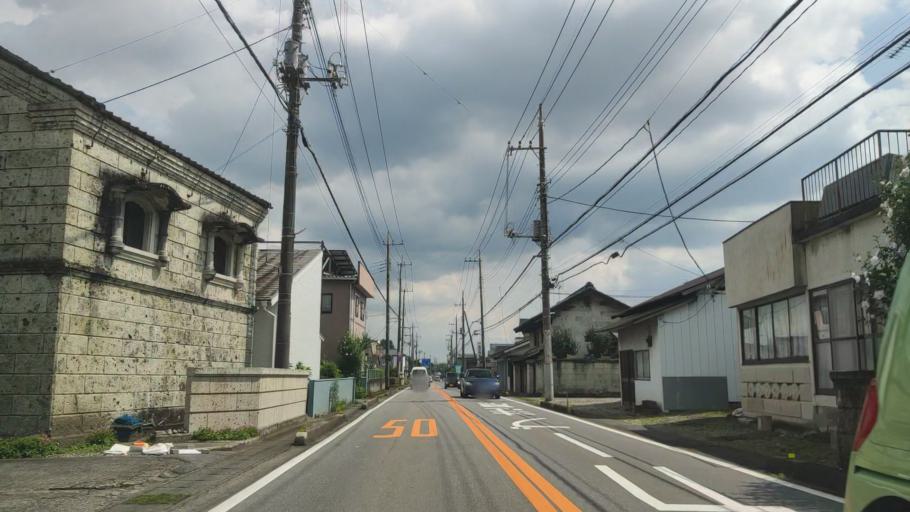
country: JP
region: Tochigi
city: Utsunomiya-shi
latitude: 36.6525
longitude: 139.8423
